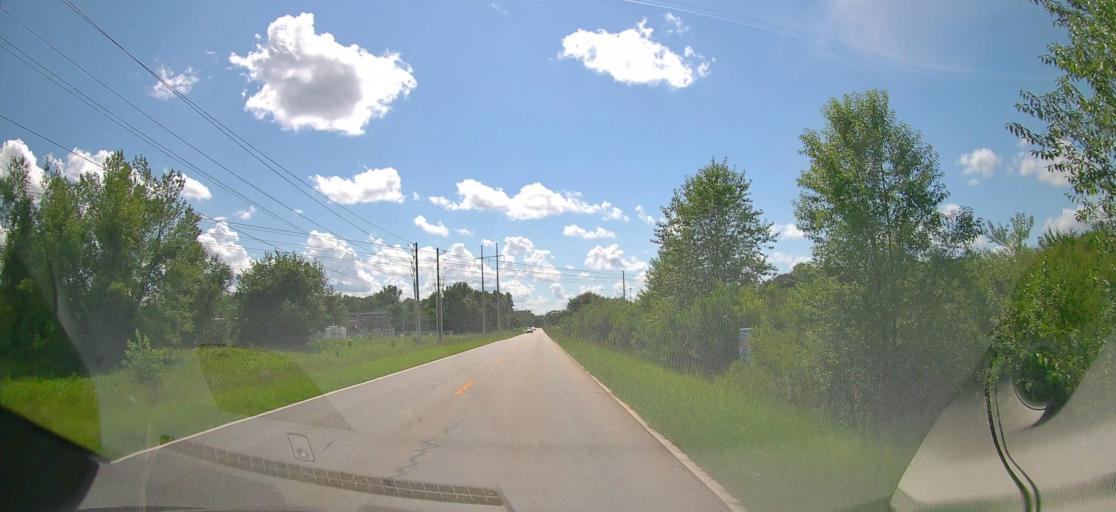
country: US
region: Georgia
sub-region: Houston County
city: Centerville
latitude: 32.6186
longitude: -83.7260
